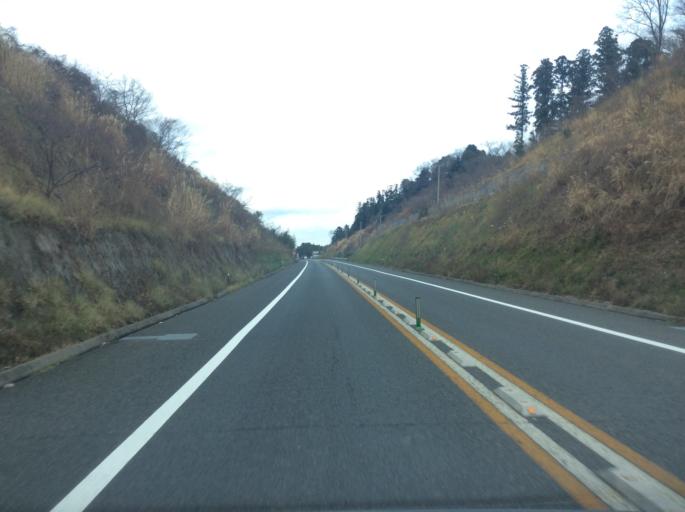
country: JP
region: Fukushima
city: Iwaki
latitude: 37.1490
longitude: 140.9653
